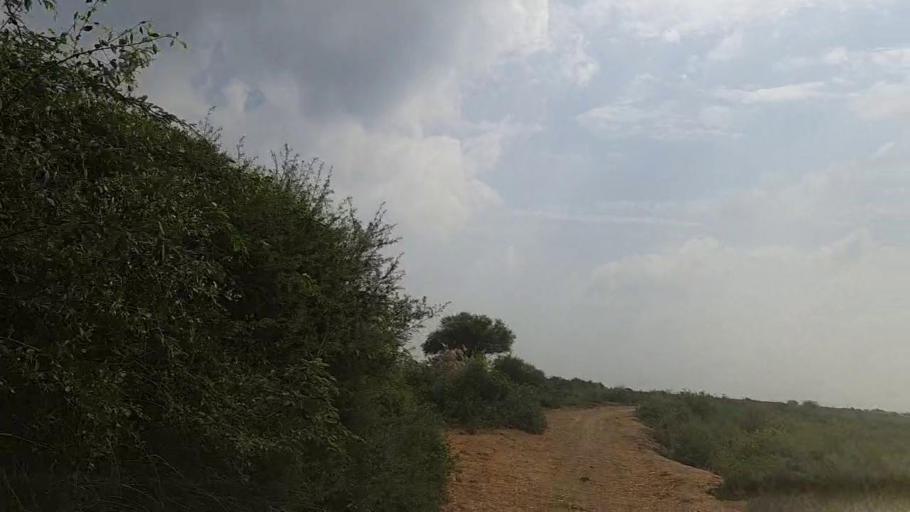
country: PK
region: Sindh
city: Mirpur Batoro
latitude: 24.6089
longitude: 68.1385
